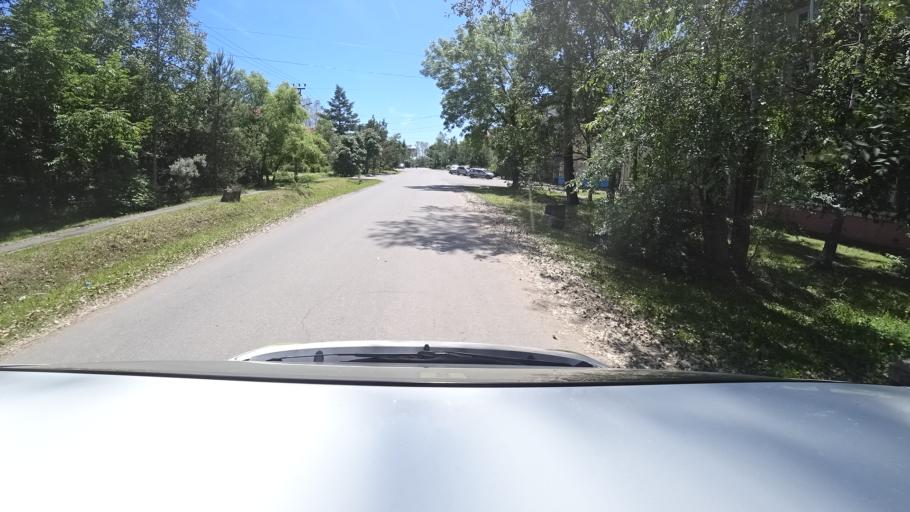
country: RU
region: Khabarovsk Krai
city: Topolevo
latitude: 48.5093
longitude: 135.1718
